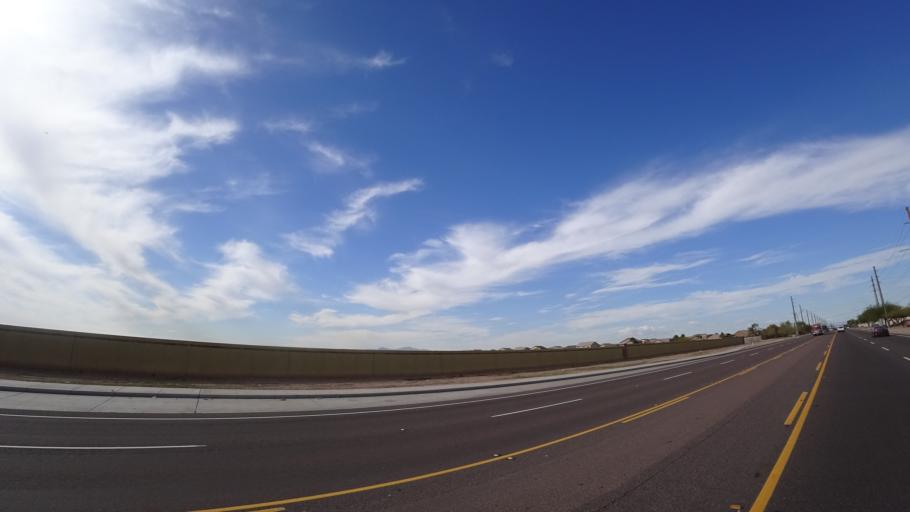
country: US
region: Arizona
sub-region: Maricopa County
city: Tolleson
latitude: 33.4410
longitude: -112.2898
